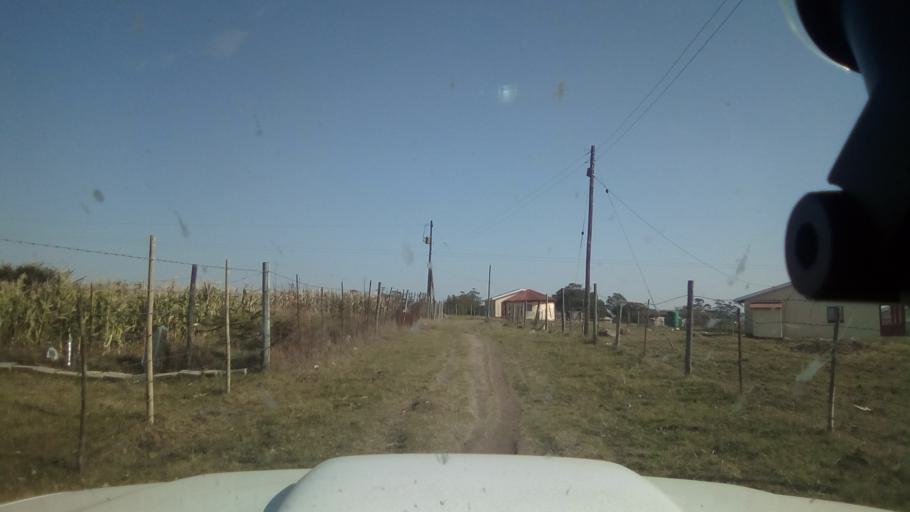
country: ZA
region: Eastern Cape
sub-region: Buffalo City Metropolitan Municipality
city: Bhisho
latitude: -32.9359
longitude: 27.3382
